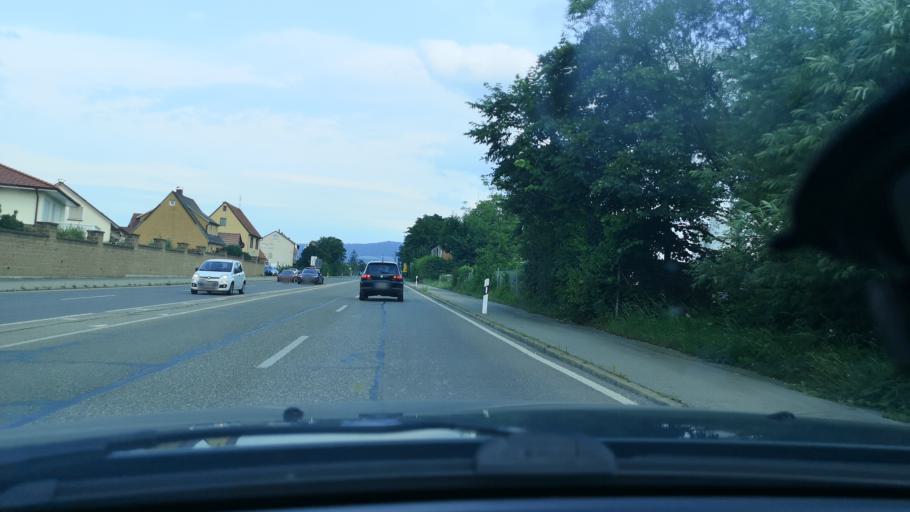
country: DE
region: Baden-Wuerttemberg
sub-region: Regierungsbezirk Stuttgart
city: Salach
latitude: 48.6875
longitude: 9.7283
